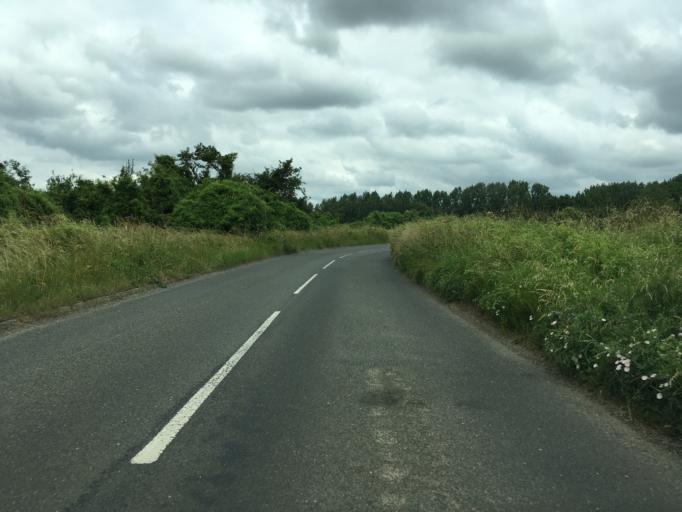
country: GB
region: England
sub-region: Oxfordshire
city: Charlbury
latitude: 51.9007
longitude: -1.4912
